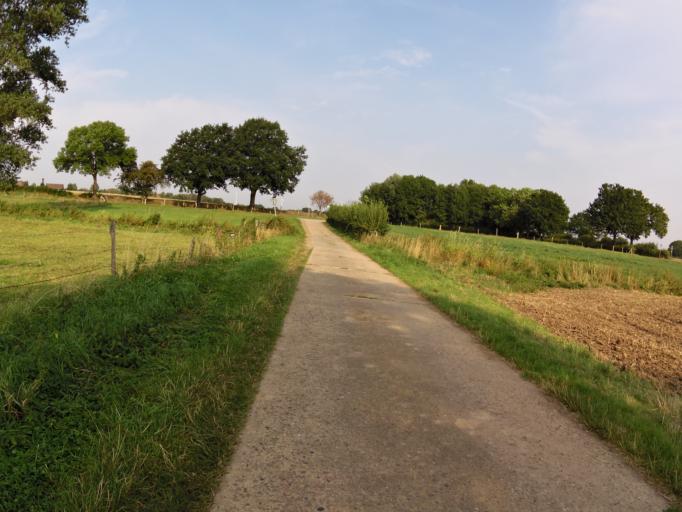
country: DE
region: Lower Saxony
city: Raddestorf
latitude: 52.4746
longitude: 9.0145
